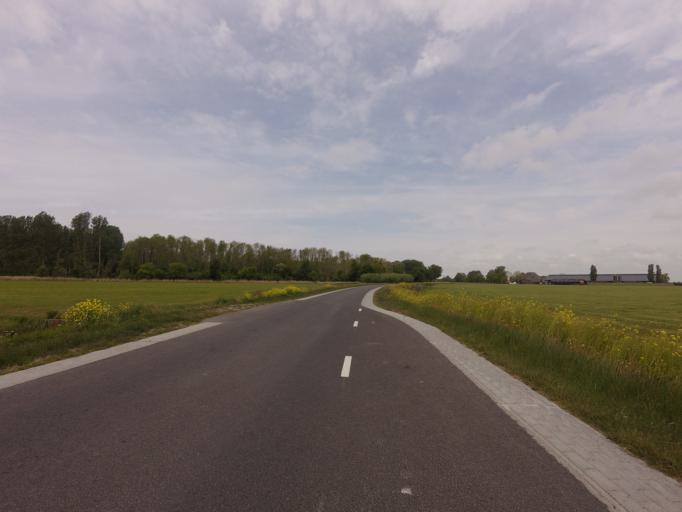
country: NL
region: Friesland
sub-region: Sudwest Fryslan
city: Bolsward
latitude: 53.0933
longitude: 5.4774
